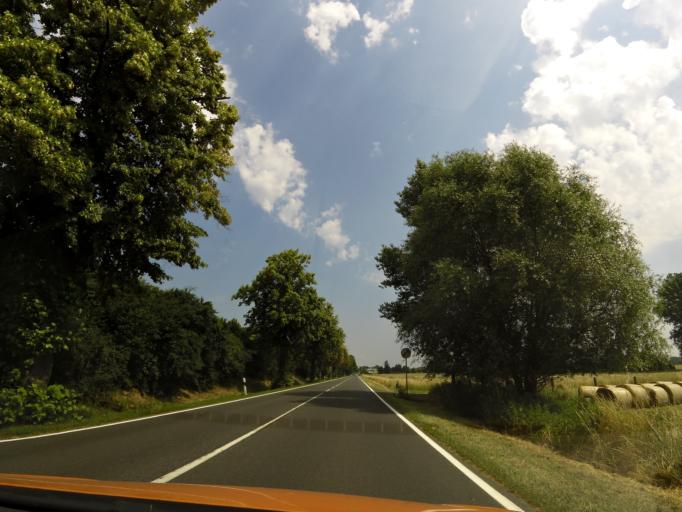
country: DE
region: Brandenburg
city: Wustermark
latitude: 52.5420
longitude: 12.9364
